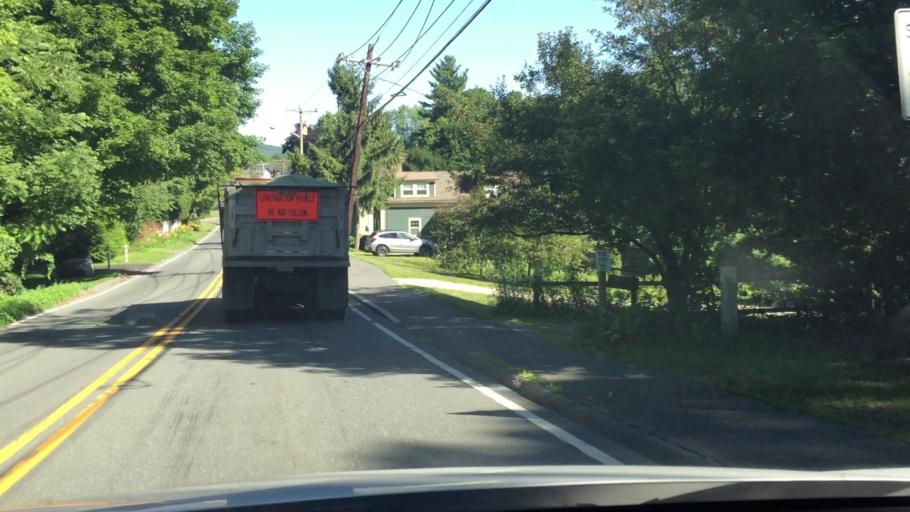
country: US
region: Massachusetts
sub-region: Berkshire County
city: West Stockbridge
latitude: 42.3308
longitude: -73.3654
